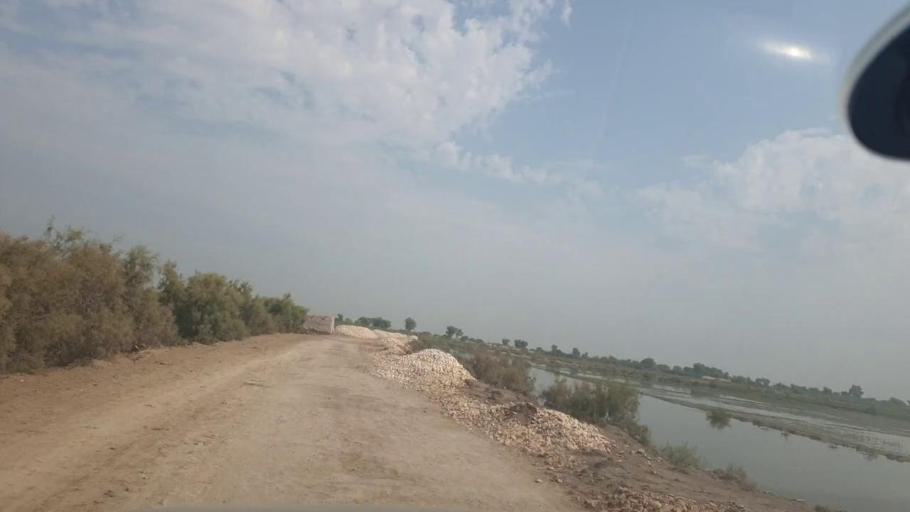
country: PK
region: Balochistan
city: Mehrabpur
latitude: 28.1125
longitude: 68.0903
